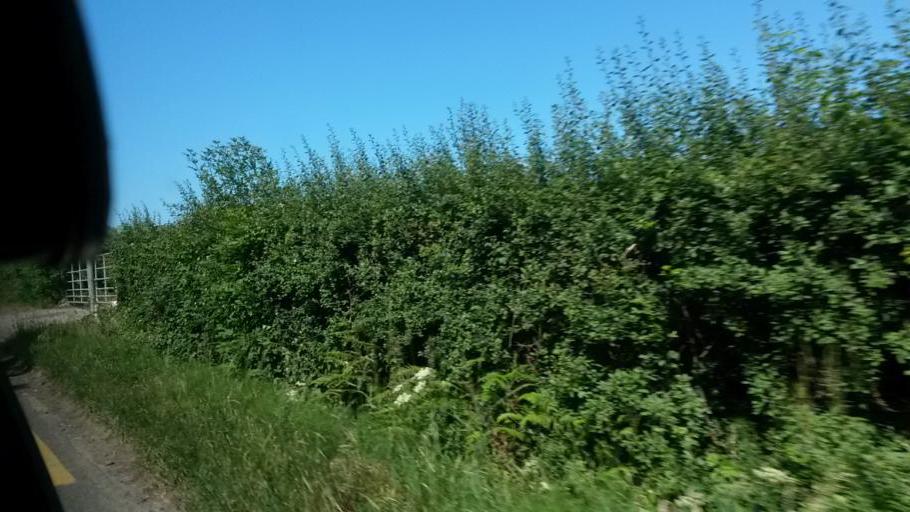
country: IE
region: Leinster
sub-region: An Mhi
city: Stamullin
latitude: 53.5499
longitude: -6.2723
